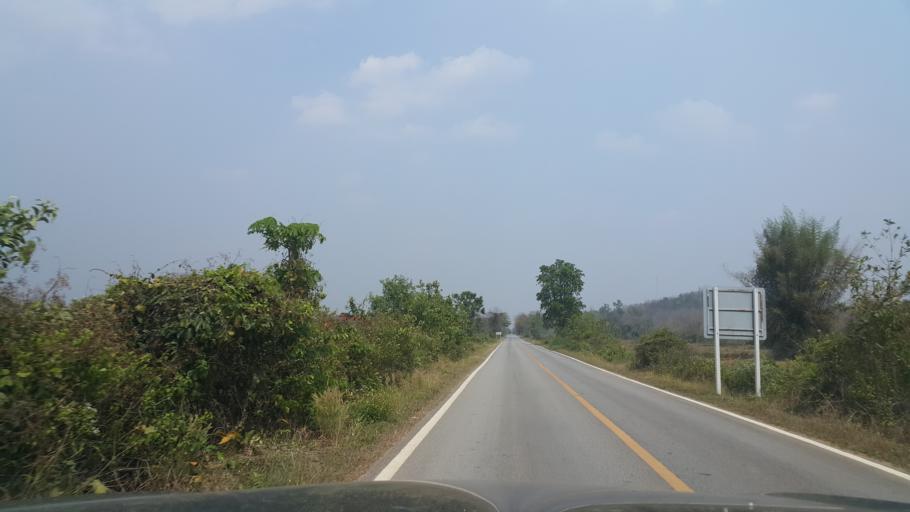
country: TH
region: Lampang
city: Soem Ngam
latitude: 18.0040
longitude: 99.1940
